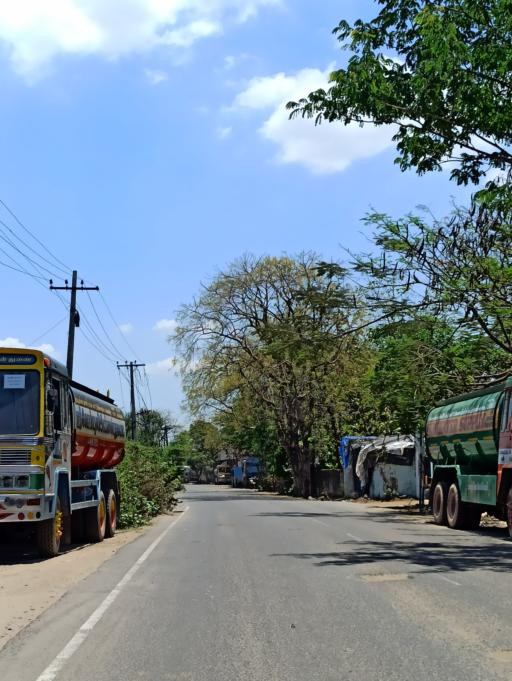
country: IN
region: Tamil Nadu
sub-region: Thiruvallur
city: Chinnasekkadu
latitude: 13.1622
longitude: 80.2299
